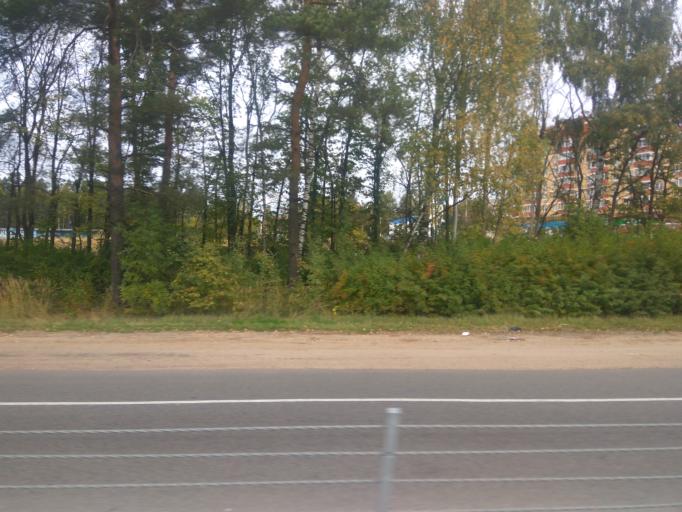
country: RU
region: Moskovskaya
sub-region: Shchelkovskiy Rayon
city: Grebnevo
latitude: 56.0057
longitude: 38.1383
